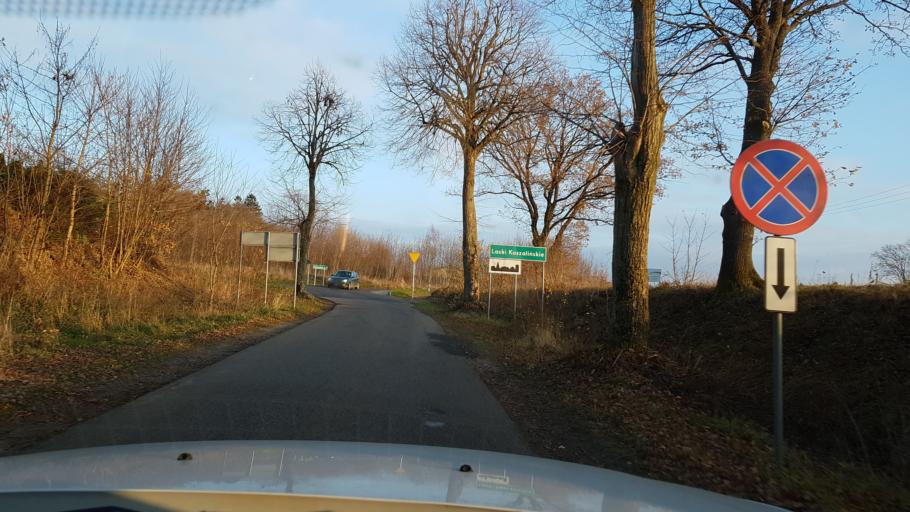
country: PL
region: West Pomeranian Voivodeship
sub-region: Koszalin
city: Koszalin
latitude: 54.1372
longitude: 16.0812
